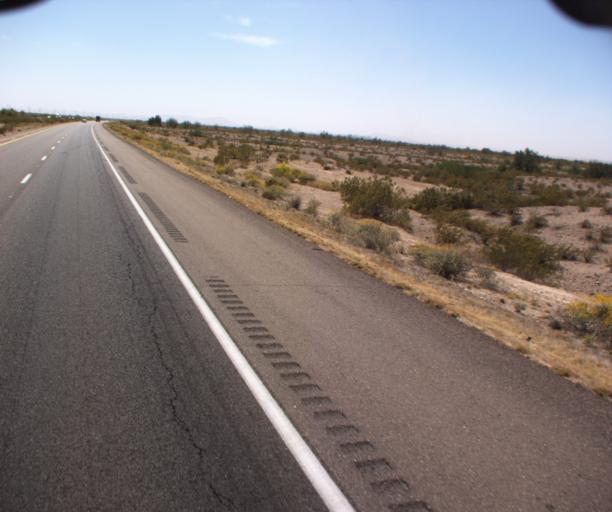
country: US
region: Arizona
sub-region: Maricopa County
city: Gila Bend
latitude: 33.0385
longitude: -112.6460
